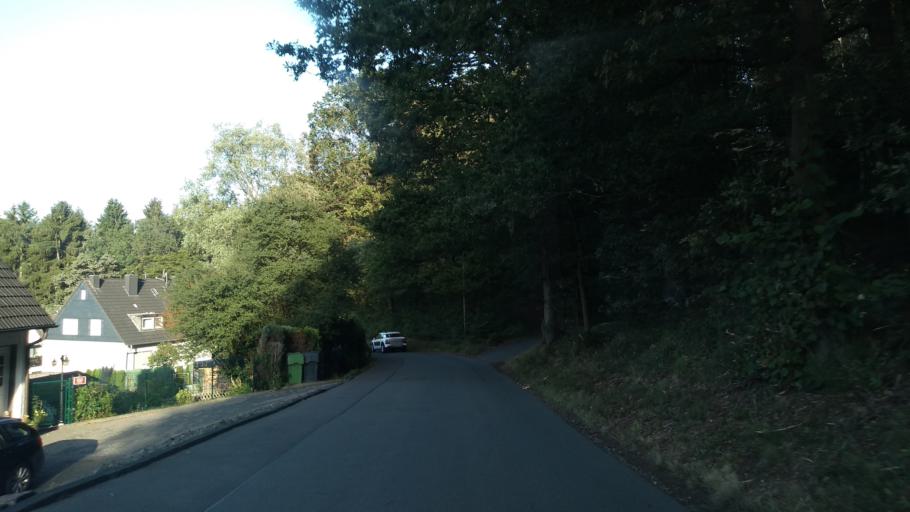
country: DE
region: North Rhine-Westphalia
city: Wiehl
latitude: 50.9670
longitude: 7.5016
